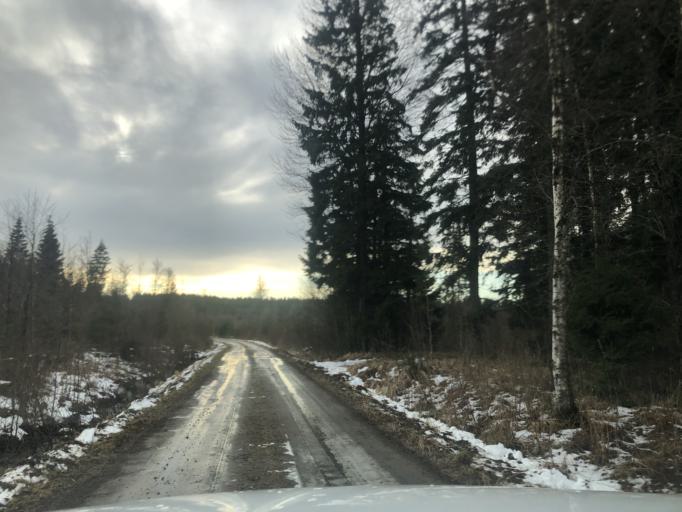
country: SE
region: Vaestra Goetaland
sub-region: Ulricehamns Kommun
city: Ulricehamn
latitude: 57.7917
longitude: 13.4856
